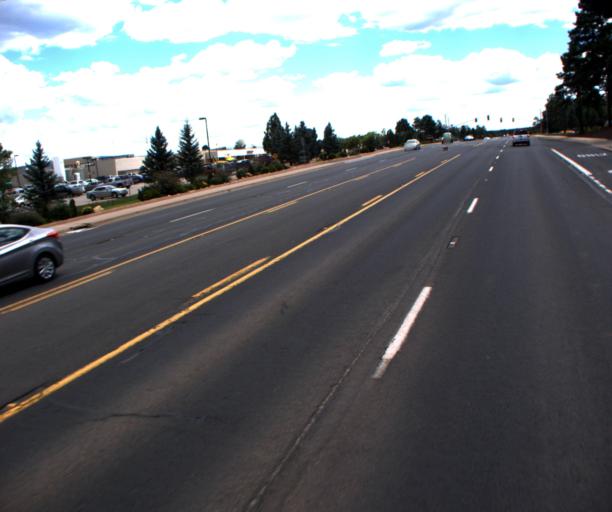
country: US
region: Arizona
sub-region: Navajo County
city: Lake of the Woods
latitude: 34.2038
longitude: -110.0201
